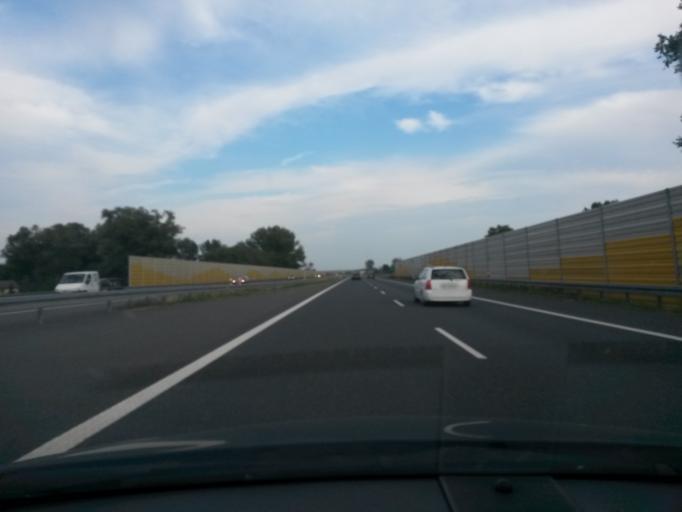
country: PL
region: Lodz Voivodeship
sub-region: Powiat poddebicki
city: Wartkowice
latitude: 52.0084
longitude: 18.9758
